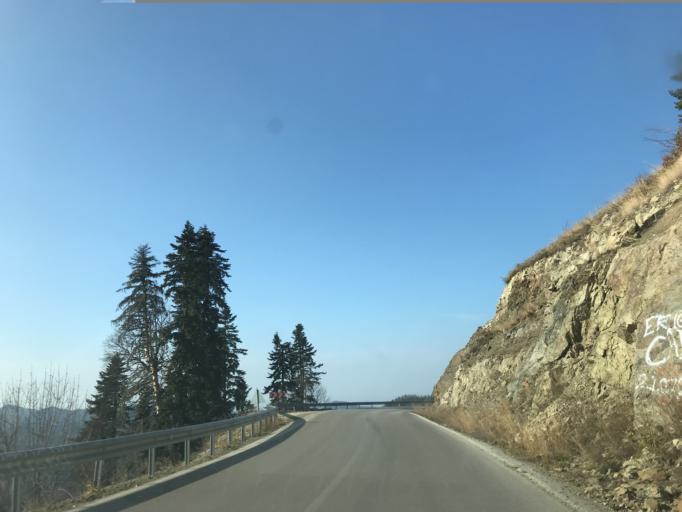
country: TR
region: Bolu
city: Bolu
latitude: 40.8841
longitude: 31.6827
